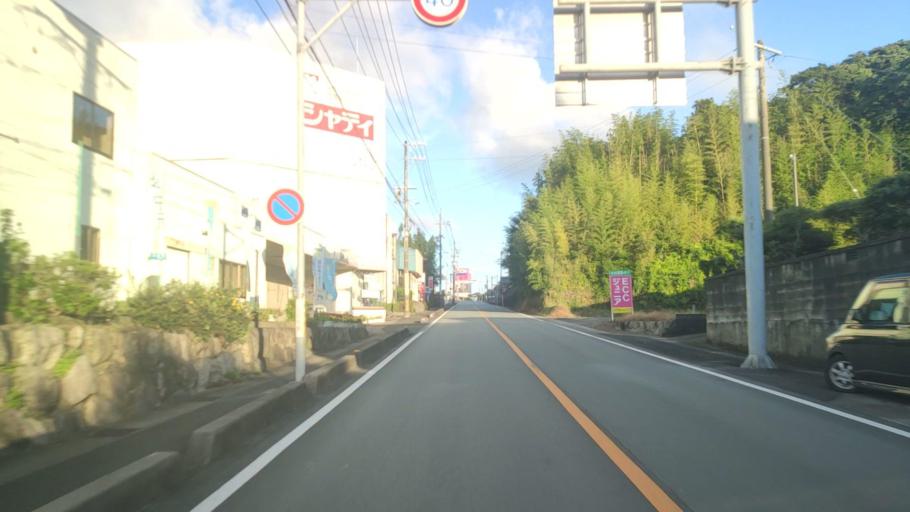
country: JP
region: Mie
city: Toba
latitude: 34.3264
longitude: 136.8250
